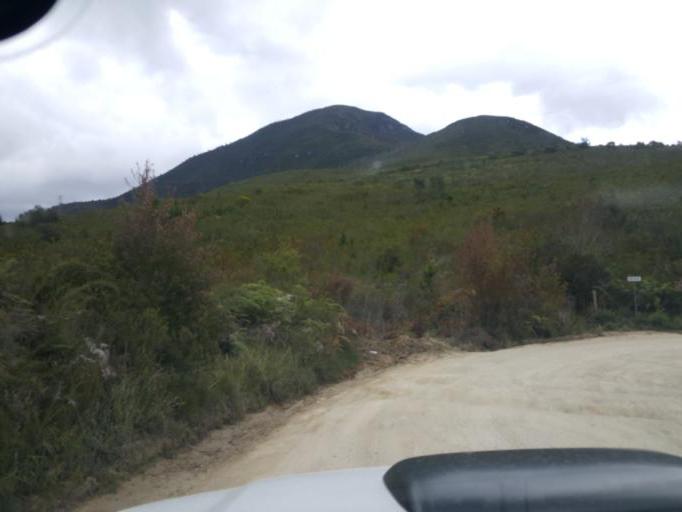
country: ZA
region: Western Cape
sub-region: Eden District Municipality
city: George
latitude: -33.9213
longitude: 22.4147
